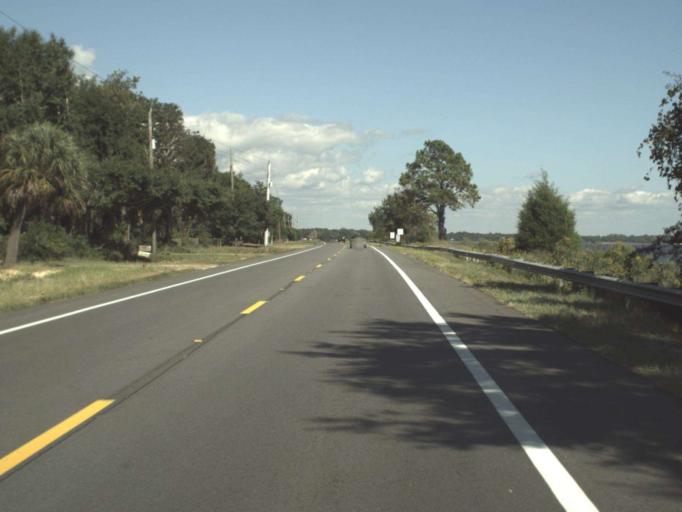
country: US
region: Florida
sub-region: Walton County
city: Miramar Beach
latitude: 30.4691
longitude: -86.3452
